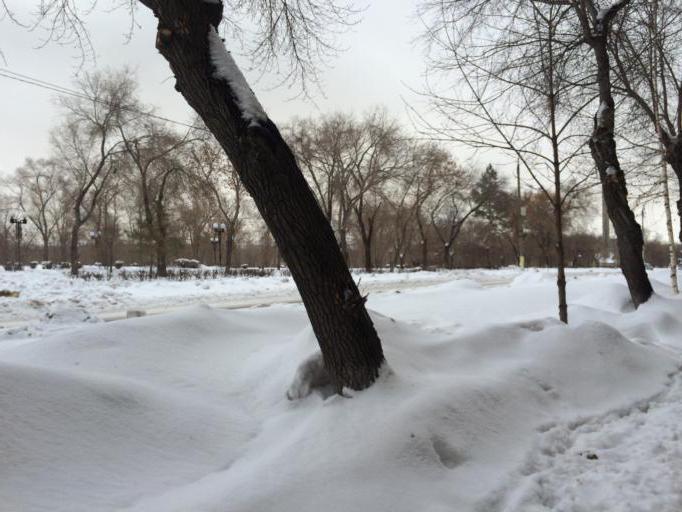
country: RU
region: Chelyabinsk
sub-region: Gorod Magnitogorsk
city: Magnitogorsk
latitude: 53.4173
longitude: 59.0012
